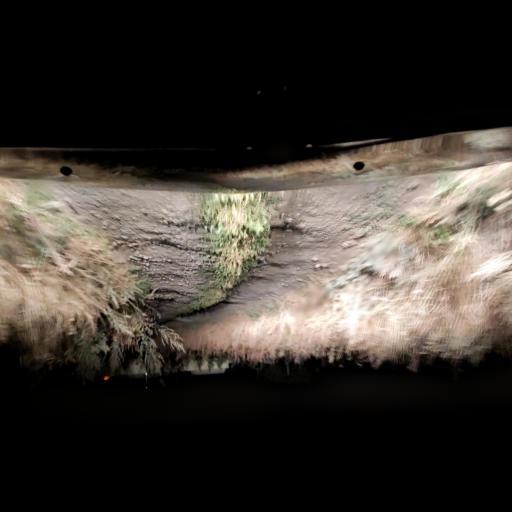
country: RU
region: Voronezj
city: Semiluki
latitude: 51.7177
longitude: 38.9943
